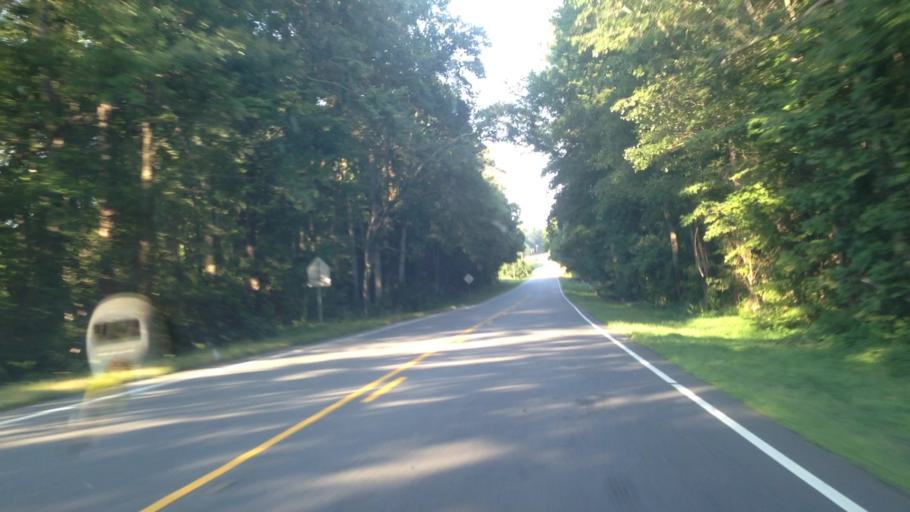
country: US
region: North Carolina
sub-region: Guilford County
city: Summerfield
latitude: 36.2628
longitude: -79.8641
